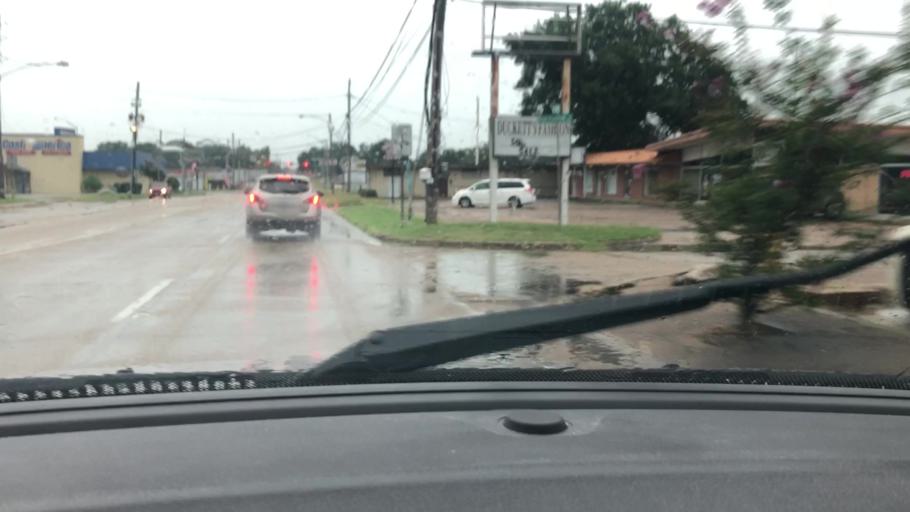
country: US
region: Texas
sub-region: Bowie County
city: Wake Village
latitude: 33.4377
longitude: -94.0804
